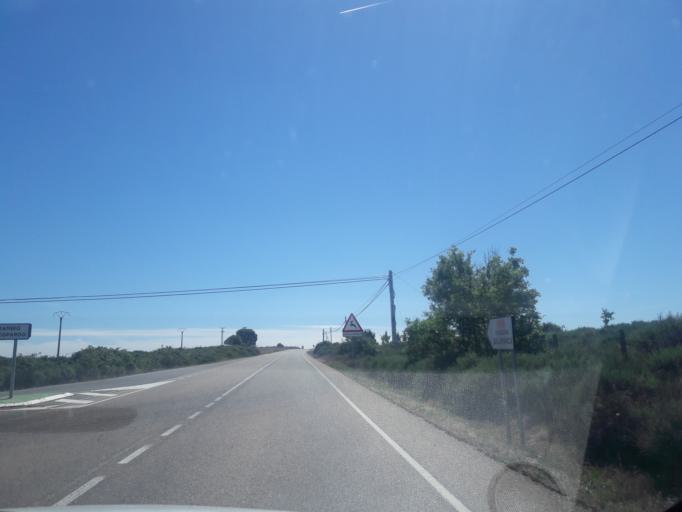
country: ES
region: Castille and Leon
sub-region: Provincia de Salamanca
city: Guadramiro
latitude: 41.0122
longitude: -6.4806
